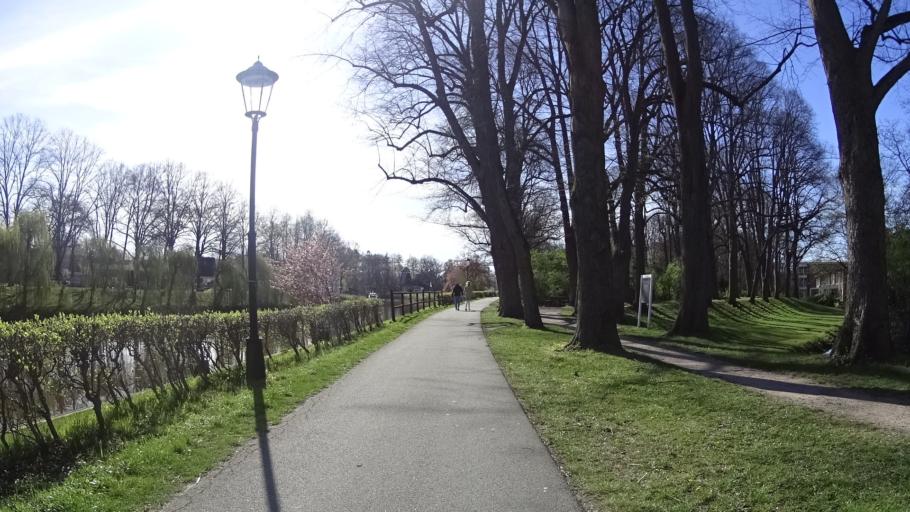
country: DE
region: Lower Saxony
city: Meppen
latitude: 52.6927
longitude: 7.2945
